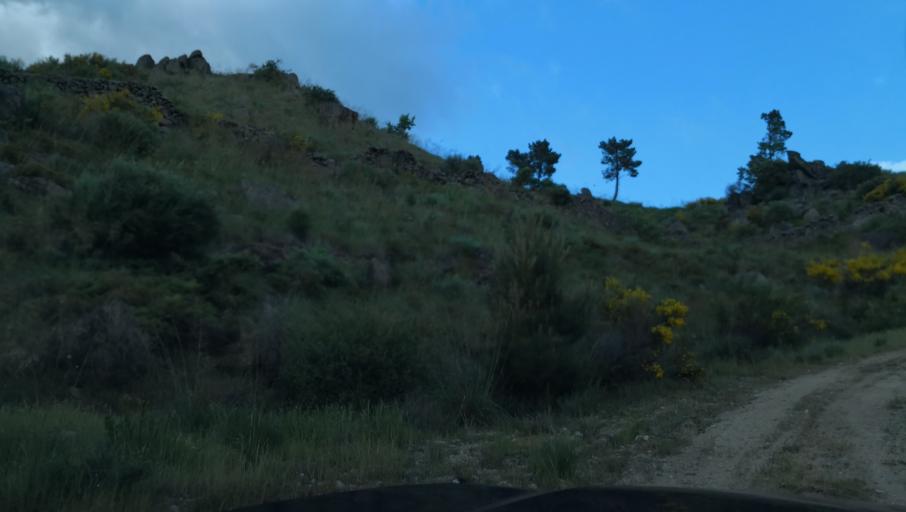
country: PT
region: Vila Real
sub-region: Vila Real
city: Vila Real
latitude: 41.2712
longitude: -7.7840
